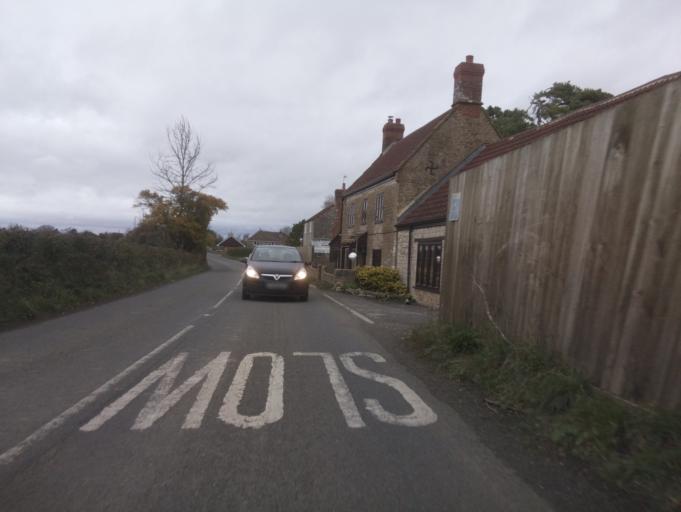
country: GB
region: England
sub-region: Dorset
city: Sherborne
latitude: 50.9901
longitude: -2.5738
